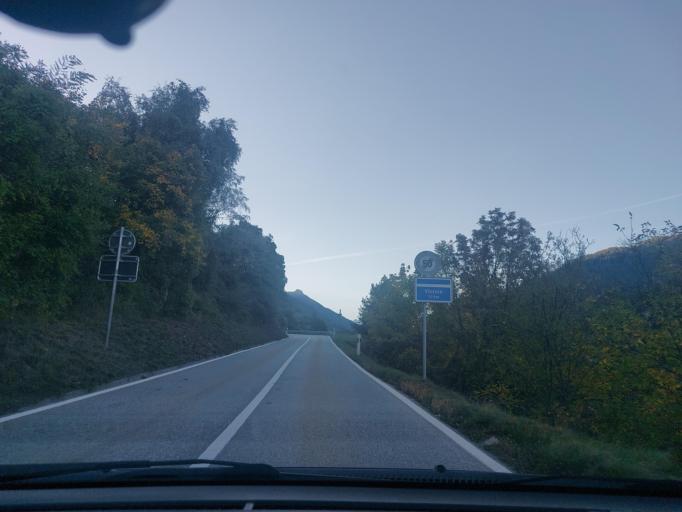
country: CH
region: Valais
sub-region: Sierre District
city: Chippis
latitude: 46.2682
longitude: 7.5538
